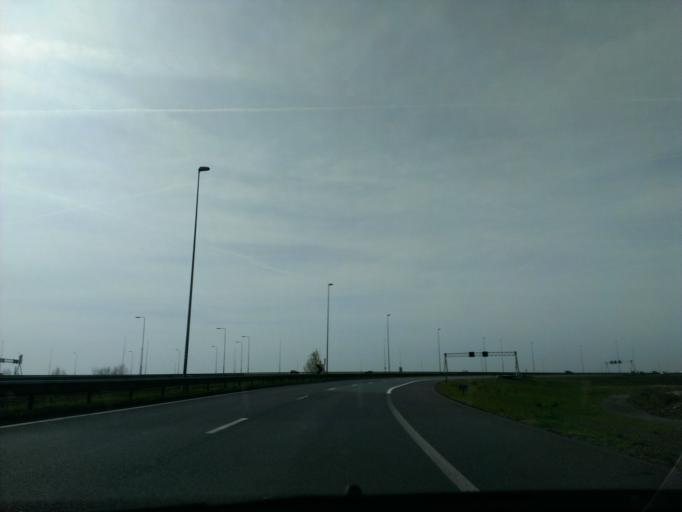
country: NL
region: North Holland
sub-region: Gemeente Amsterdam
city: Amsterdam-Zuidoost
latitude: 52.2886
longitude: 4.9435
